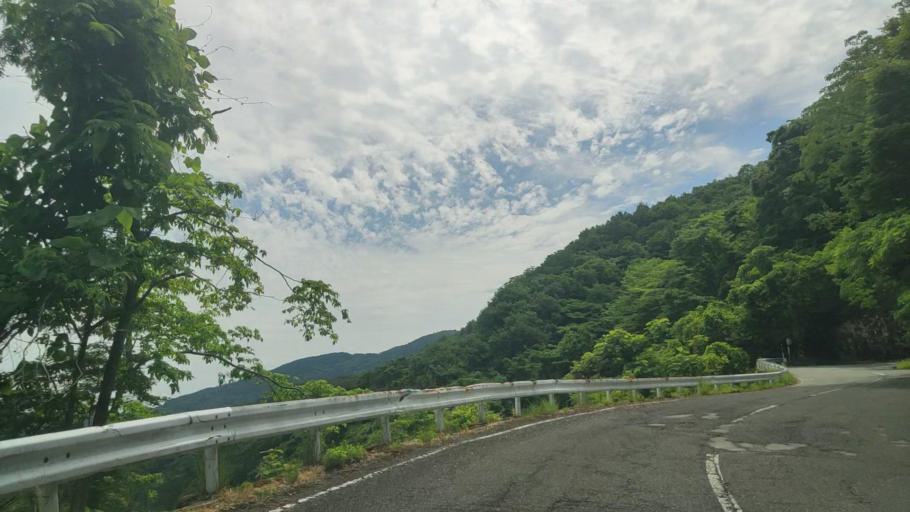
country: JP
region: Hyogo
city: Toyooka
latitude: 35.5169
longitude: 134.6870
